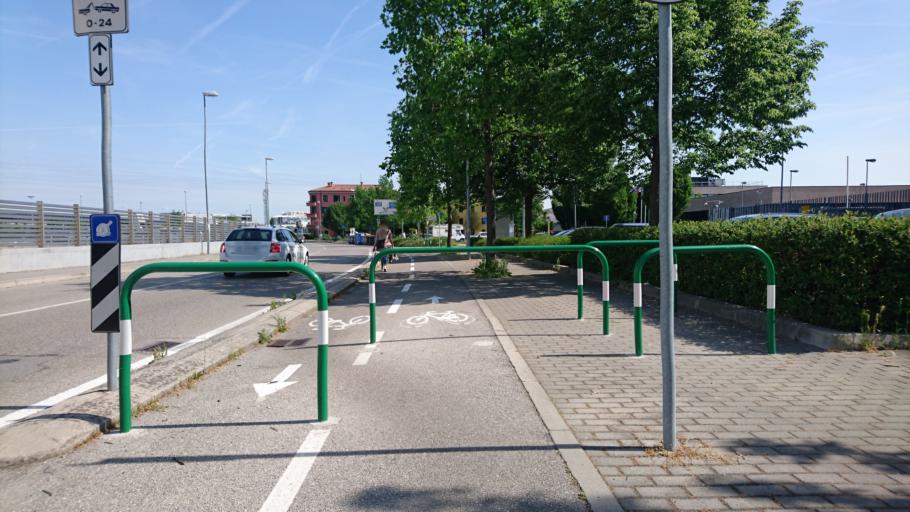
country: IT
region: Veneto
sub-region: Provincia di Padova
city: Padova
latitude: 45.4149
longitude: 11.8935
